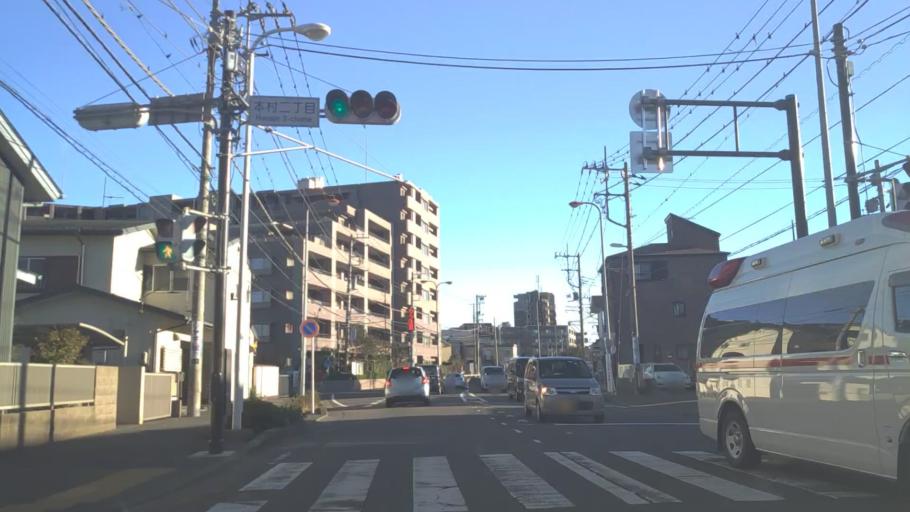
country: JP
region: Kanagawa
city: Chigasaki
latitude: 35.3348
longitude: 139.4148
